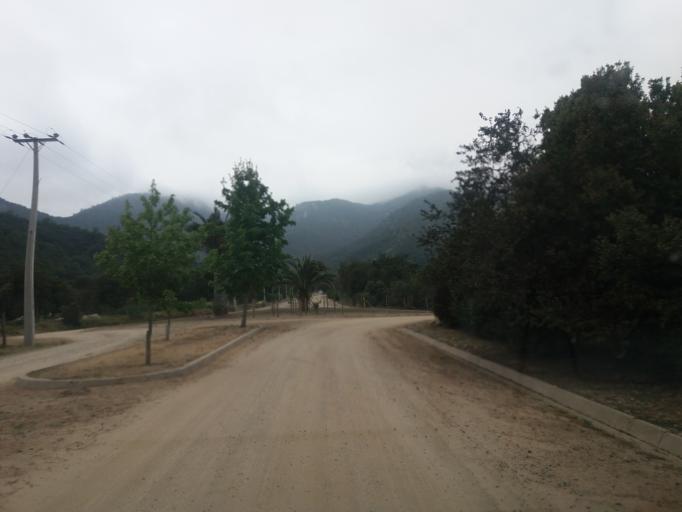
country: CL
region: Valparaiso
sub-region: Provincia de Marga Marga
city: Limache
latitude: -33.0264
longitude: -71.1323
